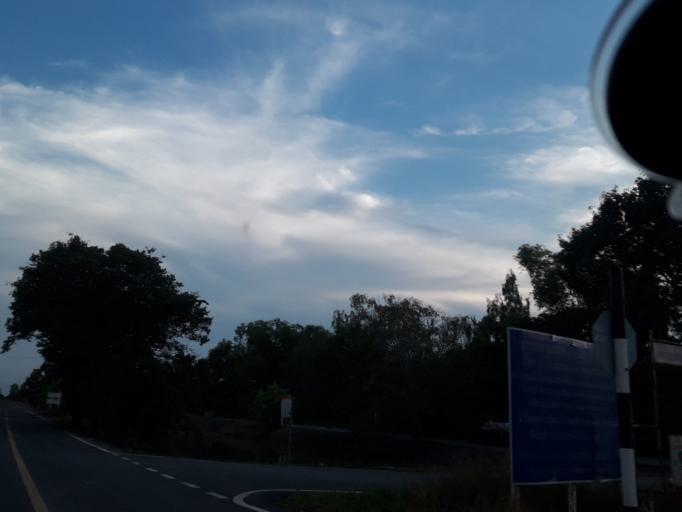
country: TH
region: Sara Buri
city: Nong Khae
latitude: 14.2650
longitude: 100.8688
